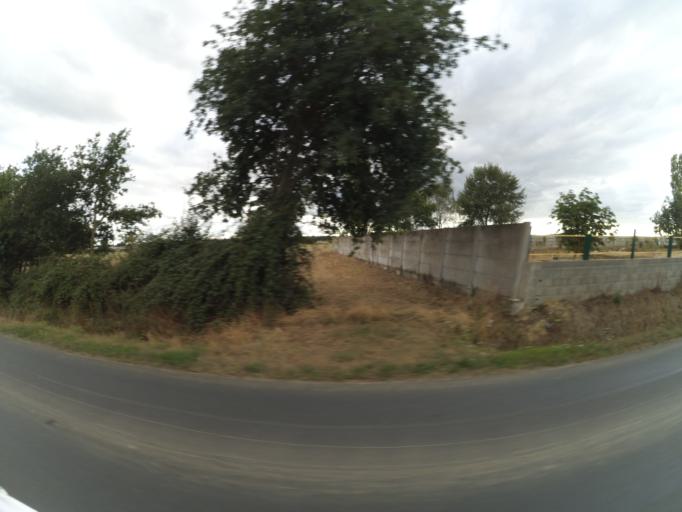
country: FR
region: Pays de la Loire
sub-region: Departement de la Vendee
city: Saint-Andre-Treize-Voies
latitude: 46.9176
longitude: -1.3877
